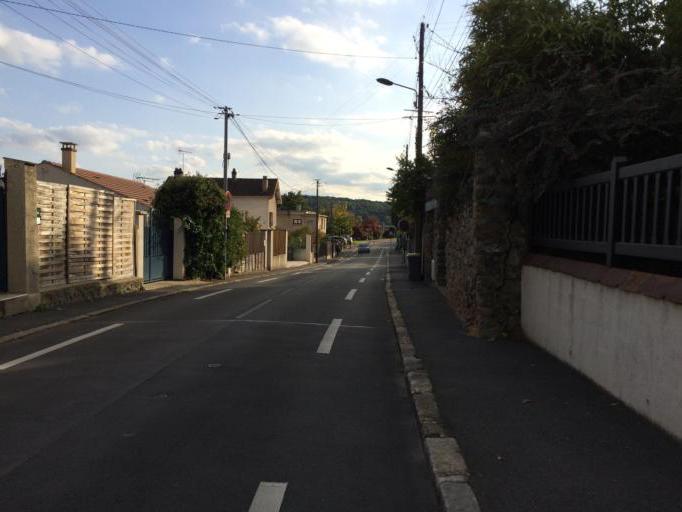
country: FR
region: Ile-de-France
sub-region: Departement de l'Essonne
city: Villebon-sur-Yvette
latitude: 48.7074
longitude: 2.2367
